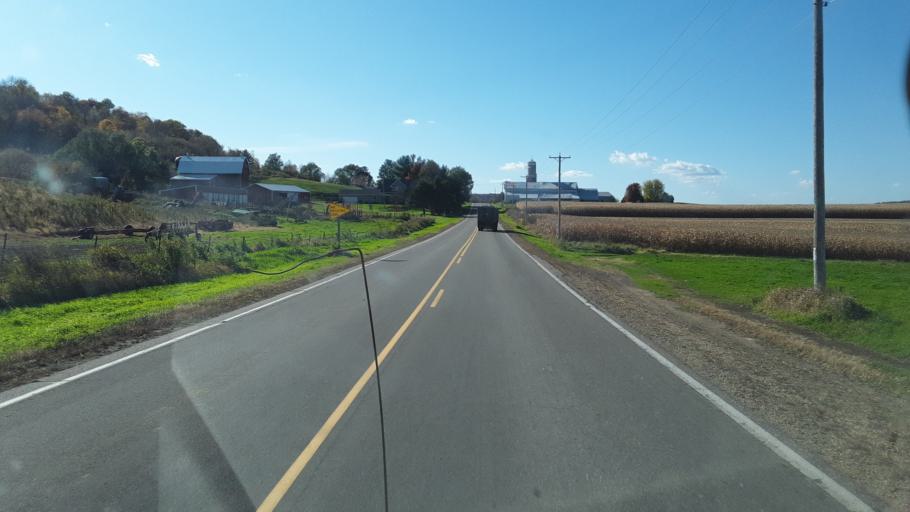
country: US
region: Wisconsin
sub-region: Sauk County
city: Reedsburg
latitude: 43.5411
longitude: -90.1498
